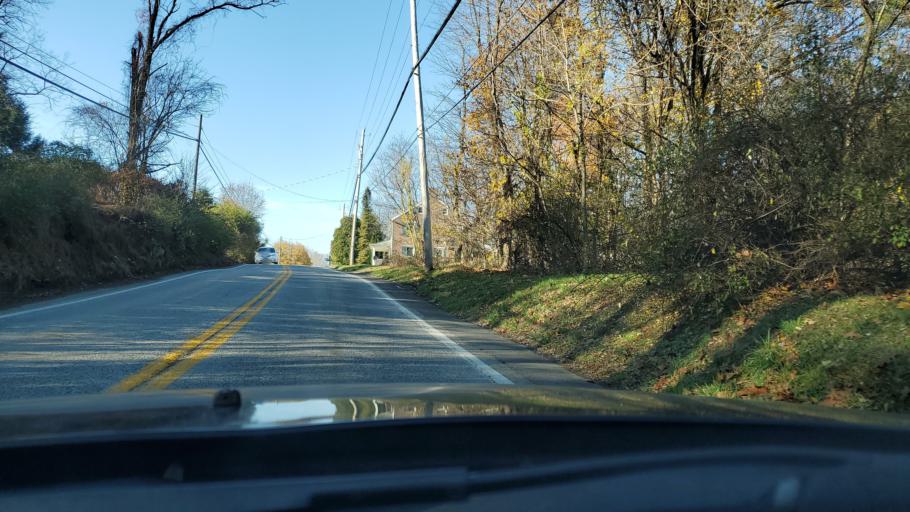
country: US
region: Pennsylvania
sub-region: Cumberland County
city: Mechanicsburg
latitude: 40.1644
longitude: -76.9851
